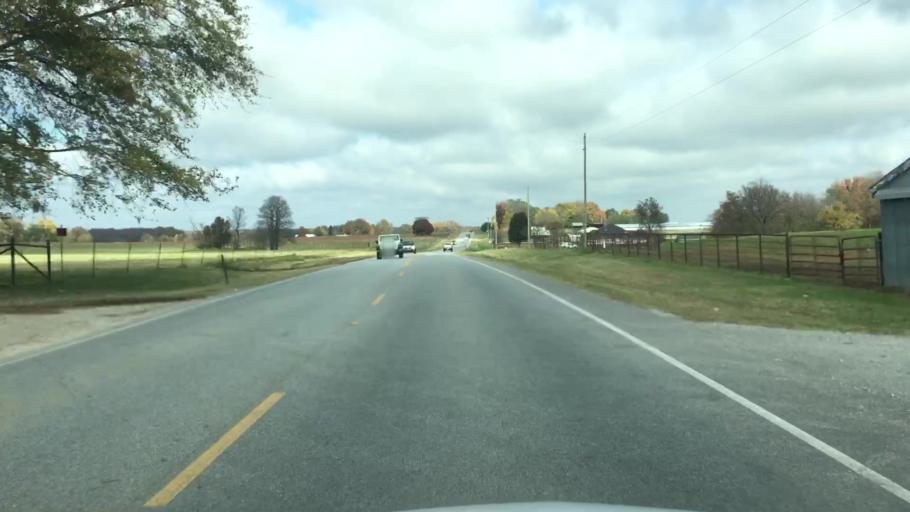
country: US
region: Arkansas
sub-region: Benton County
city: Centerton
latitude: 36.2742
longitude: -94.3502
